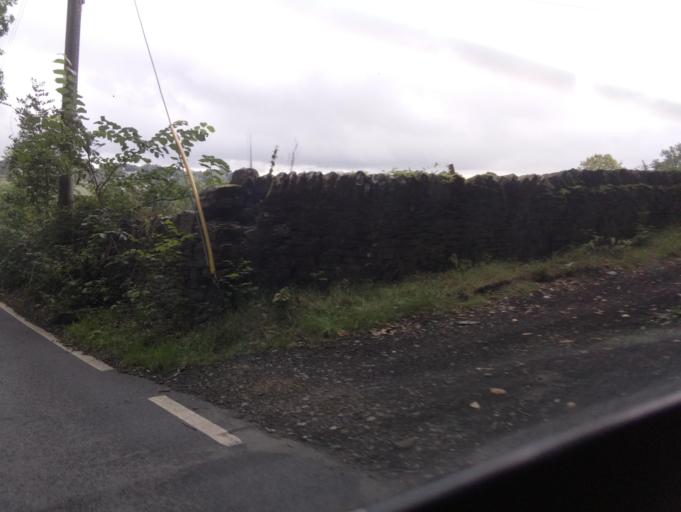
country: GB
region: England
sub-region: Kirklees
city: Shelley
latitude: 53.5873
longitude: -1.6878
